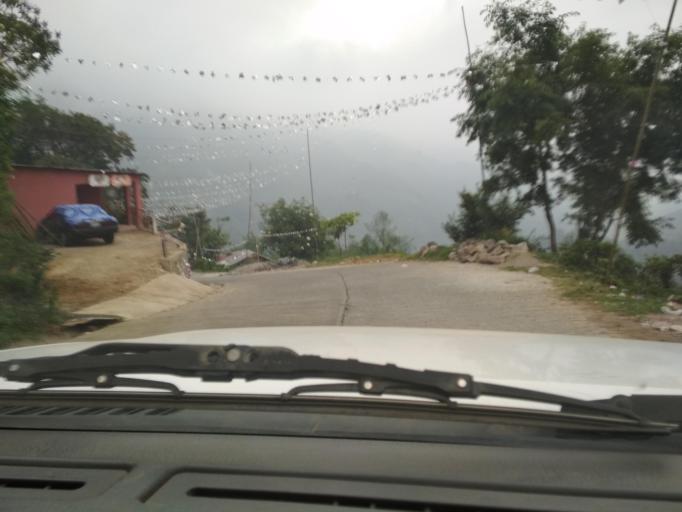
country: MX
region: Veracruz
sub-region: La Perla
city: Metlac Hernandez (Metlac Primero)
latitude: 18.9620
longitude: -97.1466
